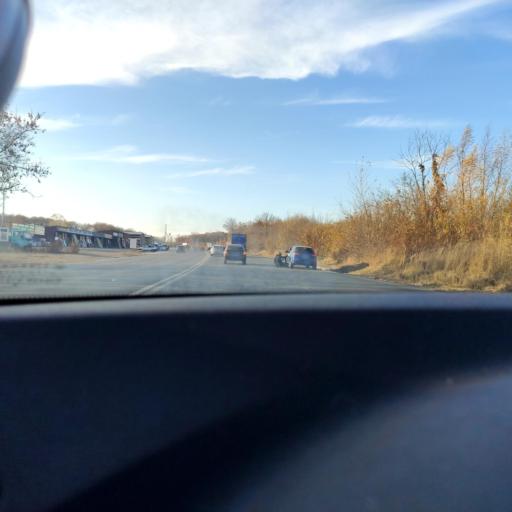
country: RU
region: Samara
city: Petra-Dubrava
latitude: 53.2706
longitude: 50.2764
